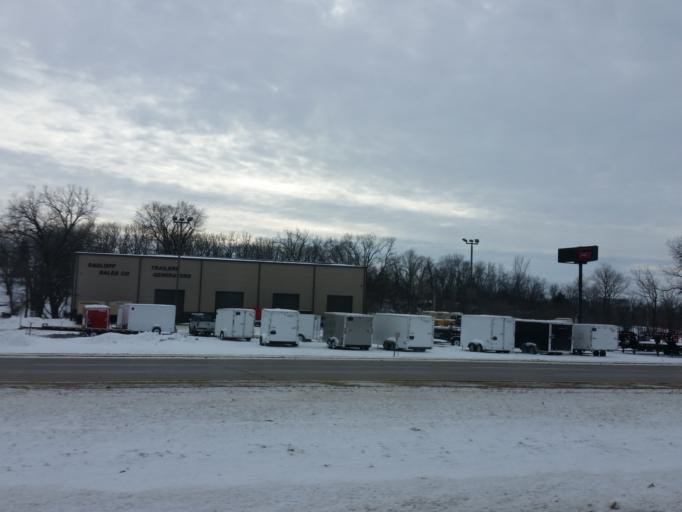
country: US
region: Iowa
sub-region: Dubuque County
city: Dyersville
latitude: 42.4693
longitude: -91.1027
